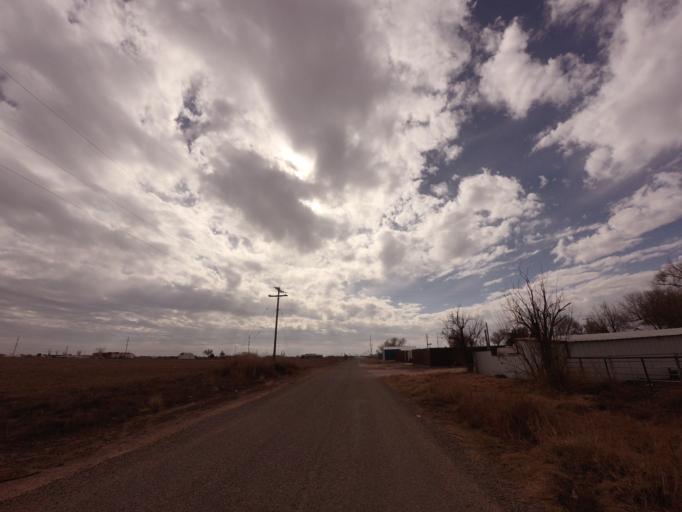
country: US
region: New Mexico
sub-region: Curry County
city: Clovis
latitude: 34.3922
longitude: -103.2142
